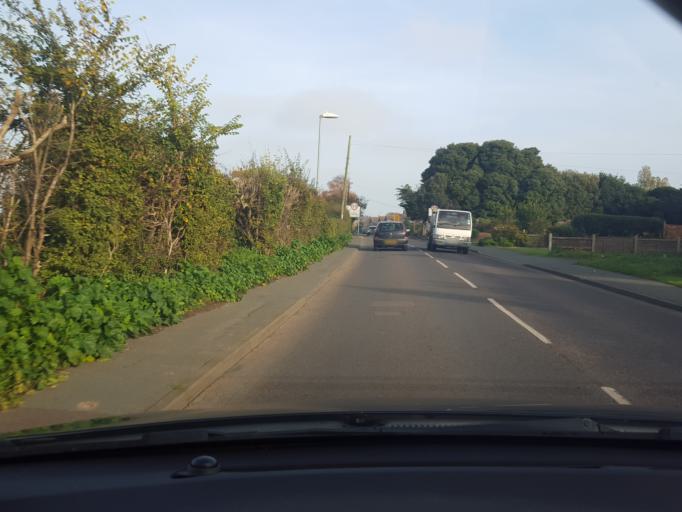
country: GB
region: England
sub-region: Essex
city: Walton-on-the-Naze
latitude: 51.8490
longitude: 1.2487
